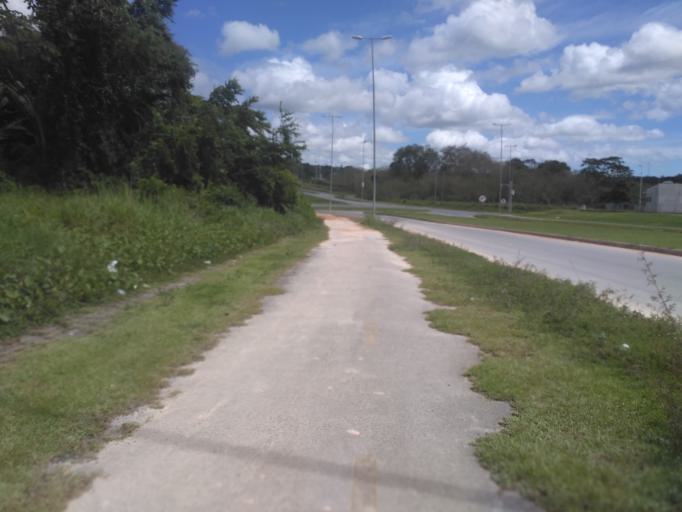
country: BR
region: Pernambuco
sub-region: Sao Lourenco Da Mata
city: Sao Lourenco da Mata
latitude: -8.0430
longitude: -35.0081
